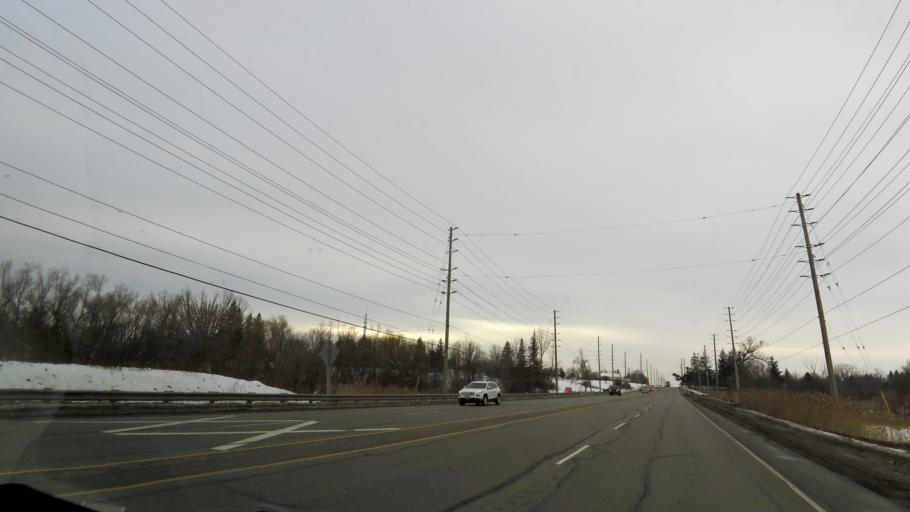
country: CA
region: Ontario
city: Vaughan
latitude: 43.8085
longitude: -79.6368
